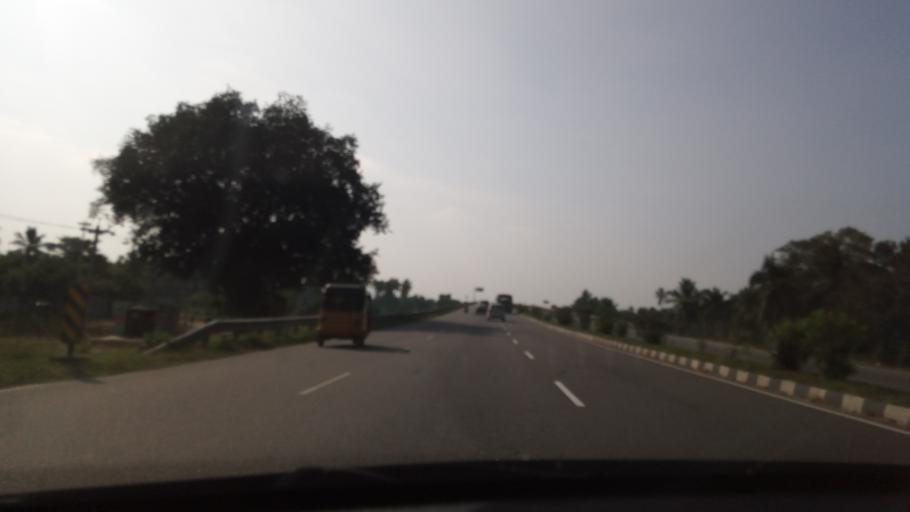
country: IN
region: Tamil Nadu
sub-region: Vellore
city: Vaniyambadi
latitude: 12.6537
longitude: 78.5944
